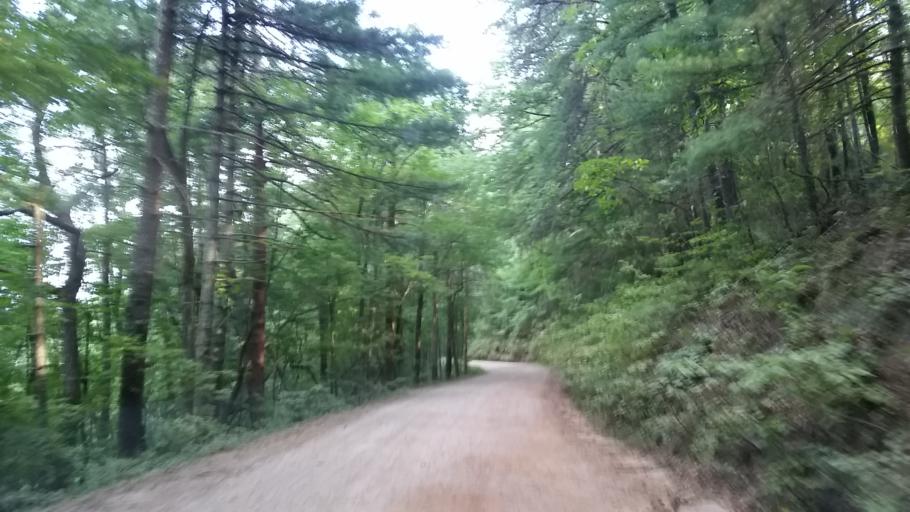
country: US
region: Georgia
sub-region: Lumpkin County
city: Dahlonega
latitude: 34.6351
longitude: -84.1005
